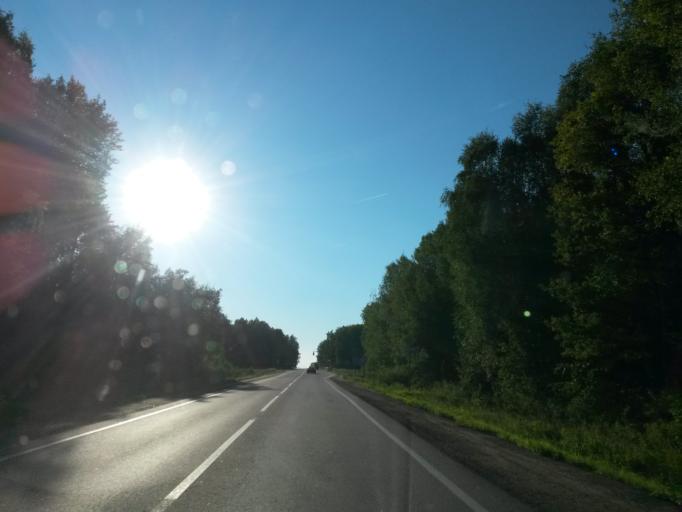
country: RU
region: Jaroslavl
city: Gavrilov-Yam
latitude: 57.2717
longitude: 39.9537
